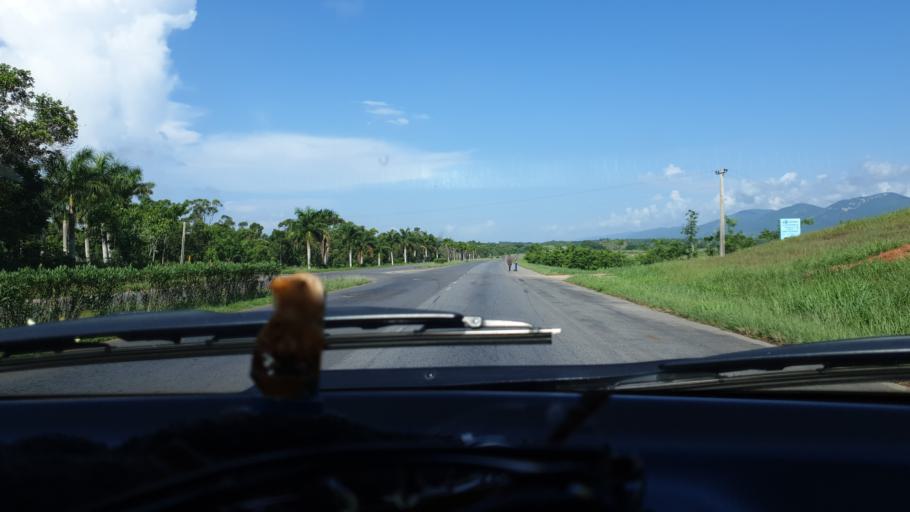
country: CU
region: Artemisa
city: San Cristobal
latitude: 22.7242
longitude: -83.0312
